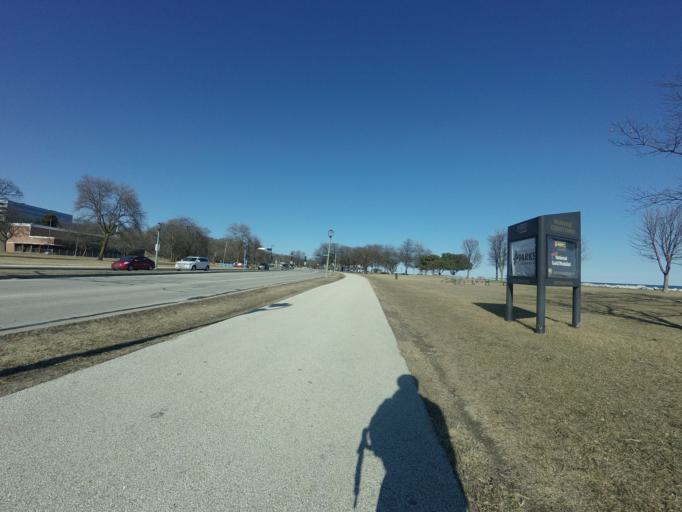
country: US
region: Wisconsin
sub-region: Milwaukee County
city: Shorewood
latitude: 43.0571
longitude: -87.8779
